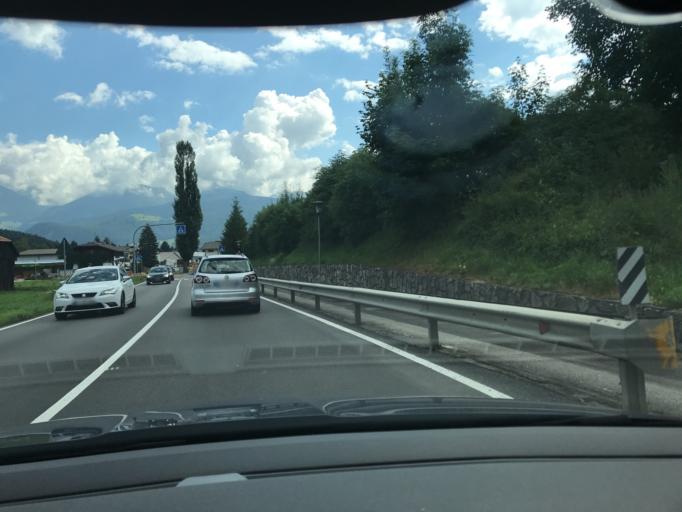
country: IT
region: Trentino-Alto Adige
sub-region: Bolzano
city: San Lorenzo di Sebato
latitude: 46.7858
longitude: 11.9109
